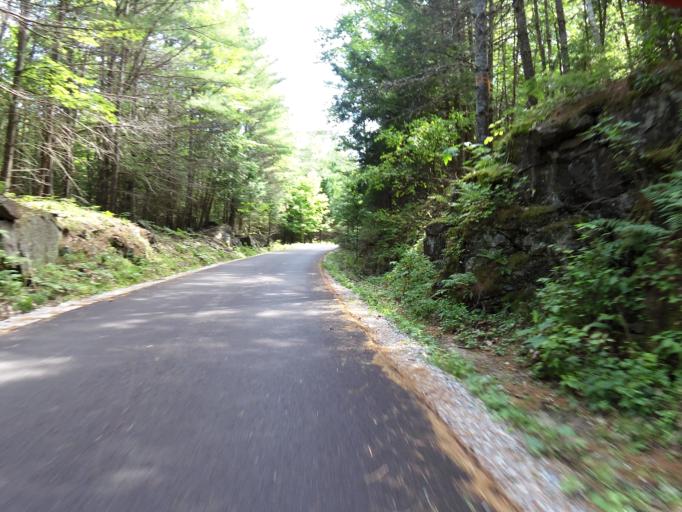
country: CA
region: Quebec
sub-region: Outaouais
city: Maniwaki
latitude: 46.1416
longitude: -76.0349
